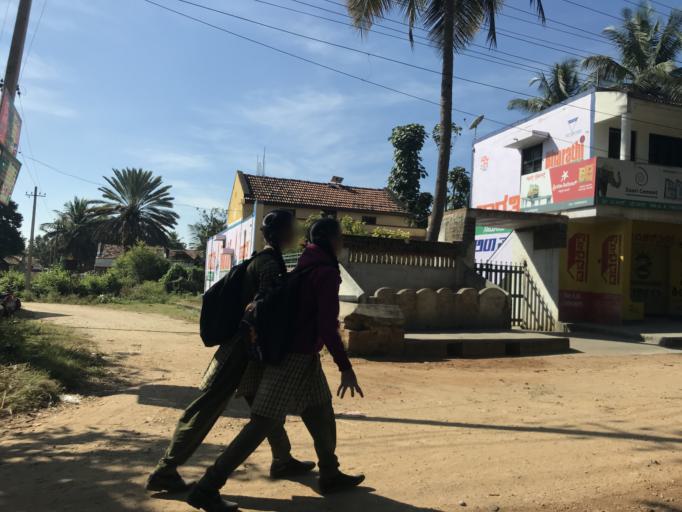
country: IN
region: Karnataka
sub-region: Mysore
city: Heggadadevankote
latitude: 12.1212
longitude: 76.4730
